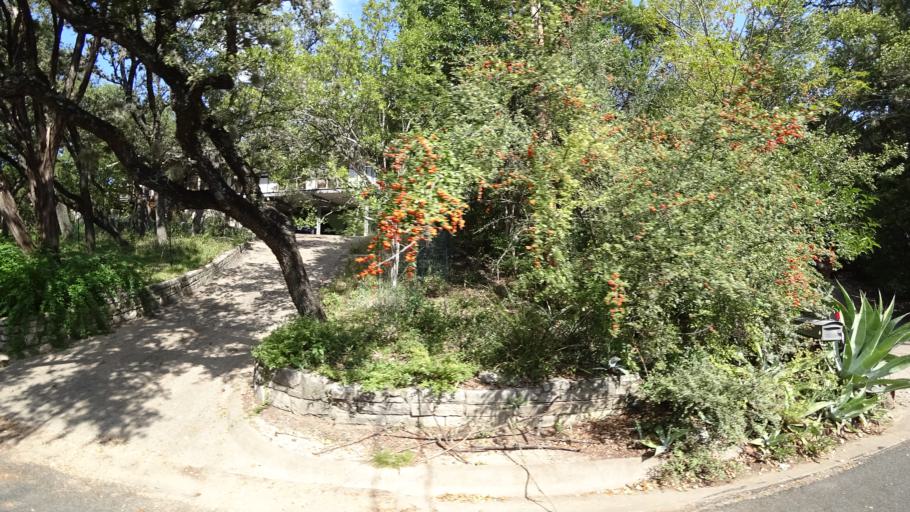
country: US
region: Texas
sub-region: Travis County
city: West Lake Hills
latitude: 30.3458
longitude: -97.7612
